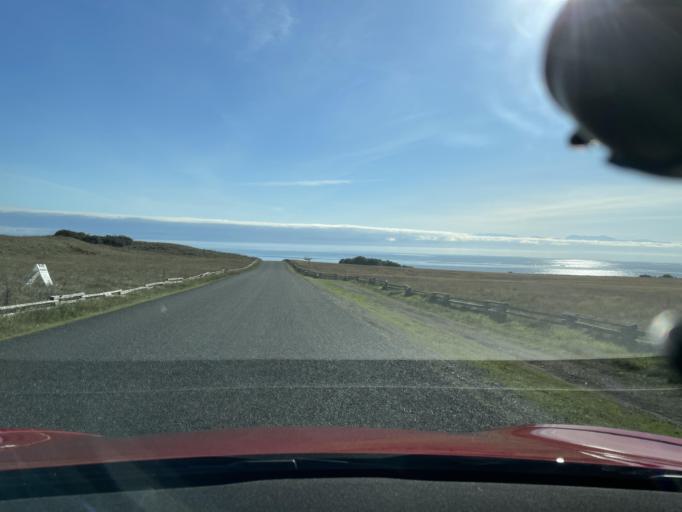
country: US
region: Washington
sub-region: San Juan County
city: Friday Harbor
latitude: 48.4607
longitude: -123.0016
